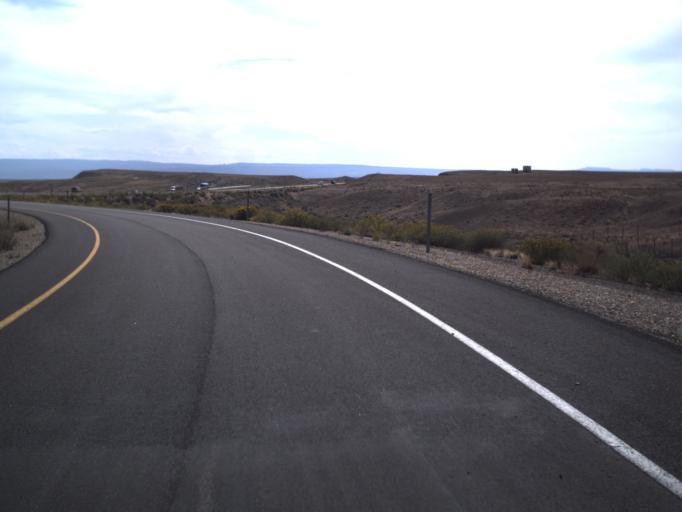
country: US
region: Colorado
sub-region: Mesa County
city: Loma
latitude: 39.0376
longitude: -109.2859
